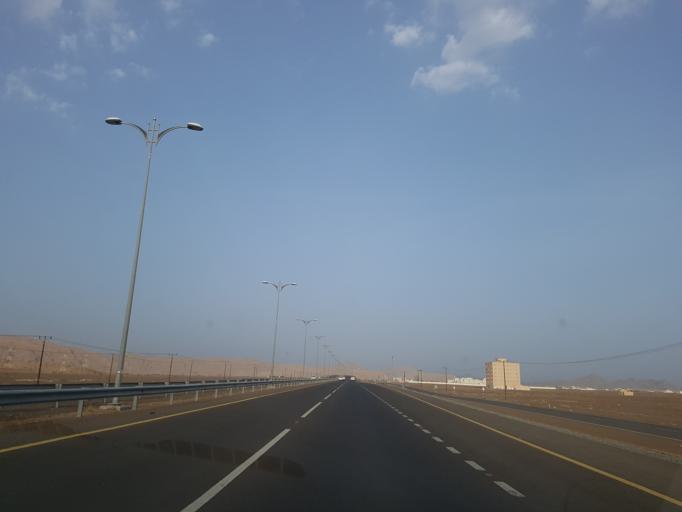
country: OM
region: Al Buraimi
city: Al Buraymi
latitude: 24.2375
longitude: 55.8993
